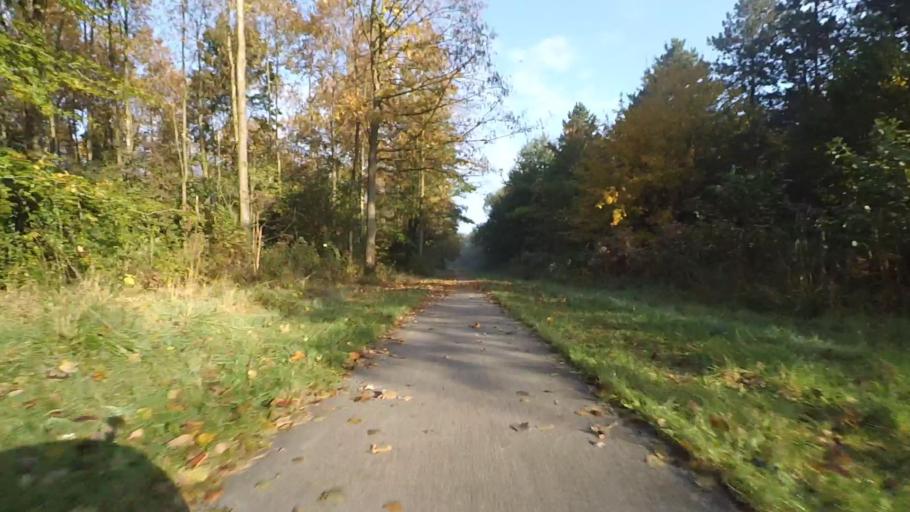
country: NL
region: Flevoland
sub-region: Gemeente Zeewolde
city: Zeewolde
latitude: 52.2963
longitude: 5.5315
